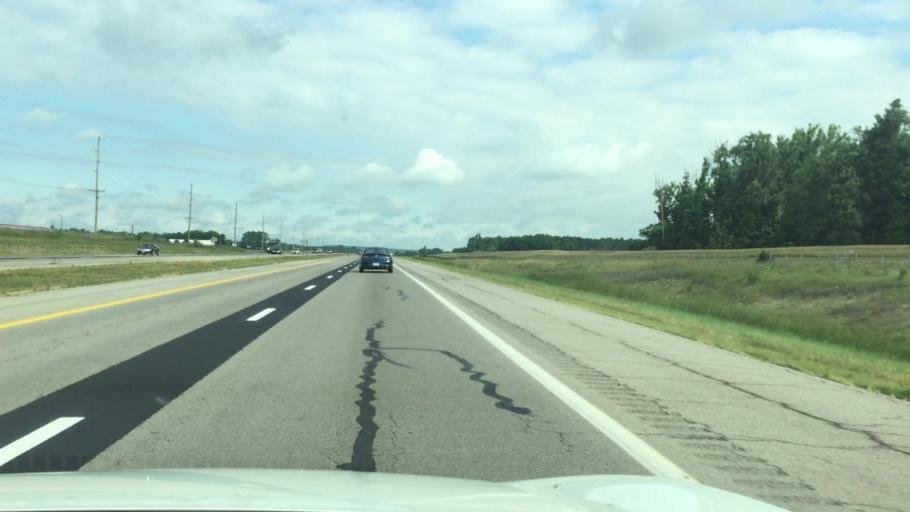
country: US
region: Ohio
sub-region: Champaign County
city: North Lewisburg
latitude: 40.2958
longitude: -83.5579
